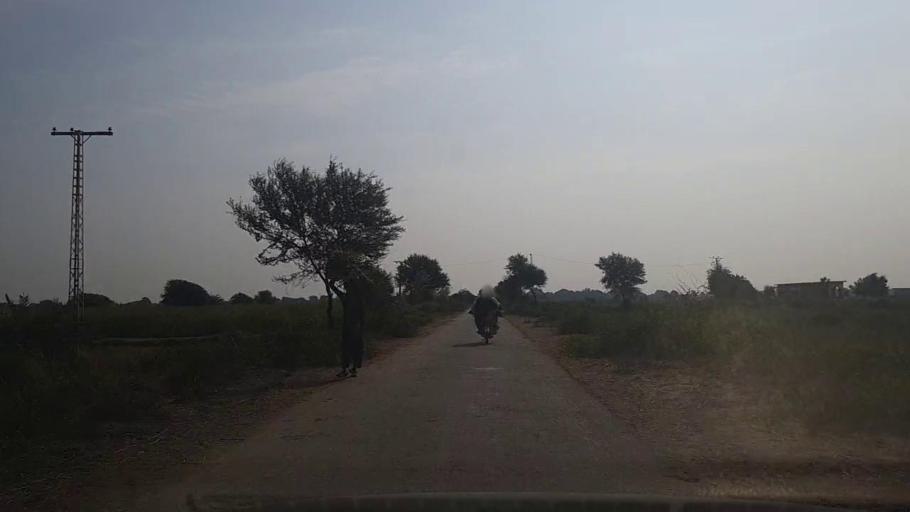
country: PK
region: Sindh
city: Bulri
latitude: 24.9730
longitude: 68.3257
